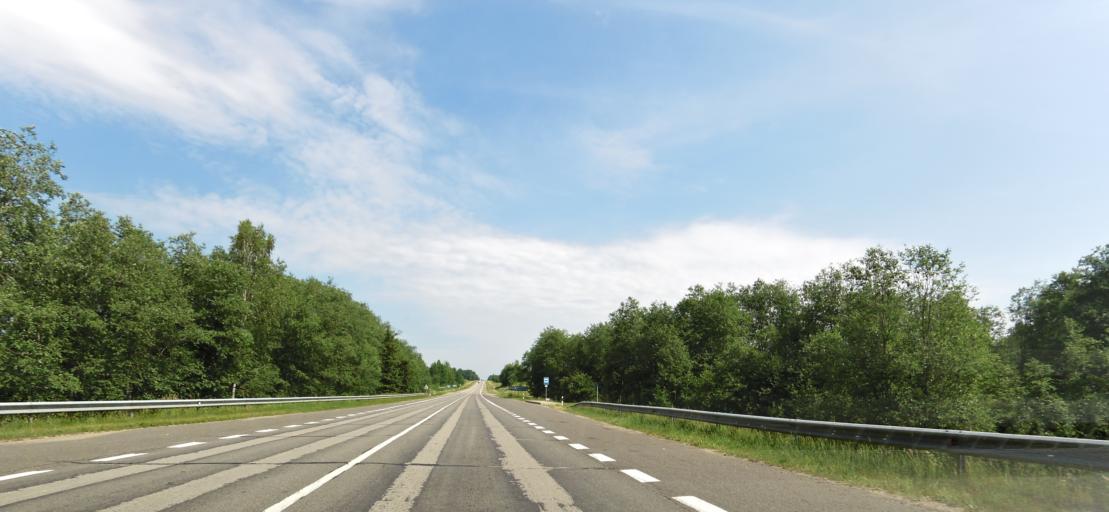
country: LT
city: Nemencine
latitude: 54.9063
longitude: 25.3231
